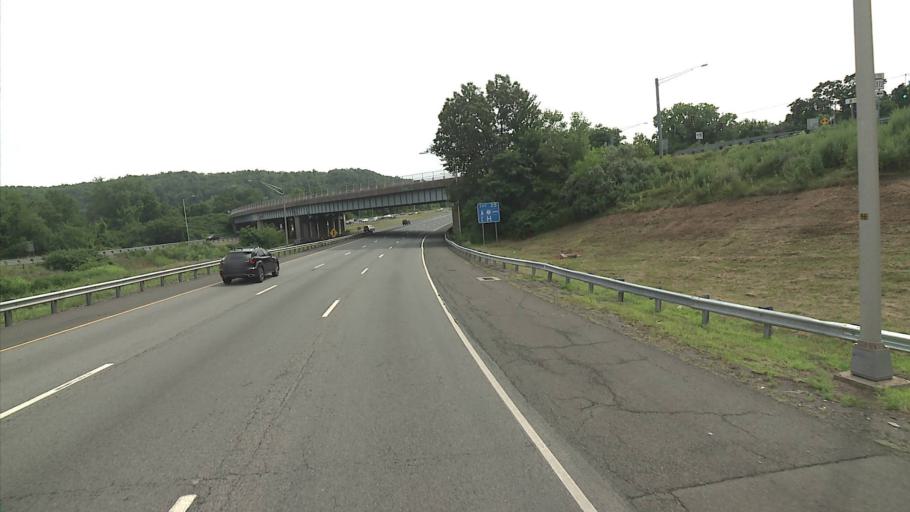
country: US
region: Connecticut
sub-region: Hartford County
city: Plainville
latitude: 41.6696
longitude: -72.8423
